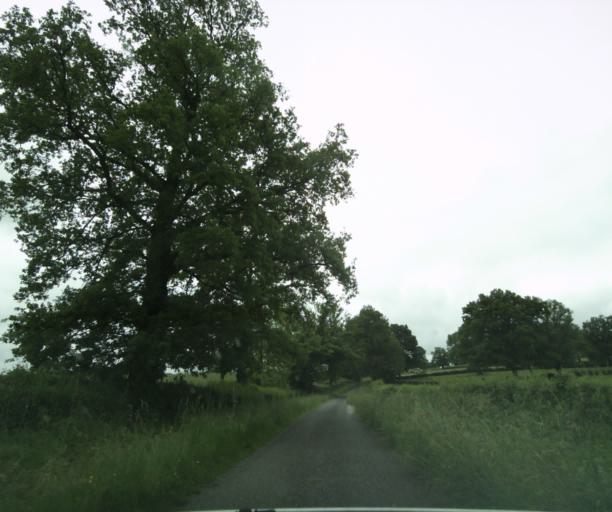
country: FR
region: Bourgogne
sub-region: Departement de Saone-et-Loire
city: Charolles
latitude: 46.4558
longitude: 4.3339
